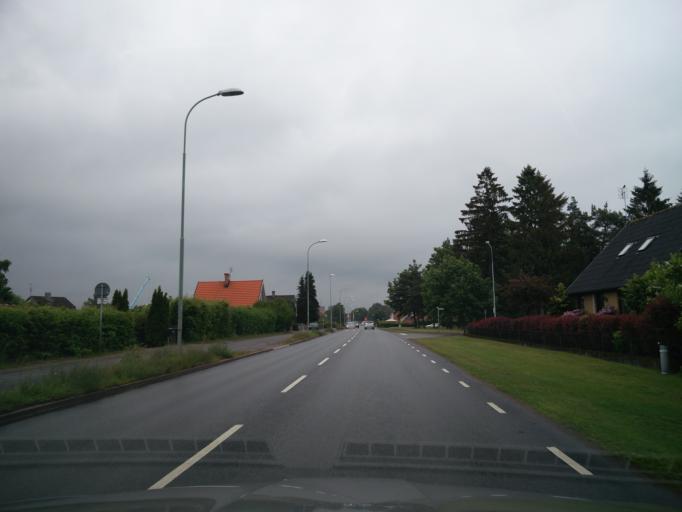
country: SE
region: Skane
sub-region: Hassleholms Kommun
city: Vinslov
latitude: 56.1019
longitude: 13.8979
